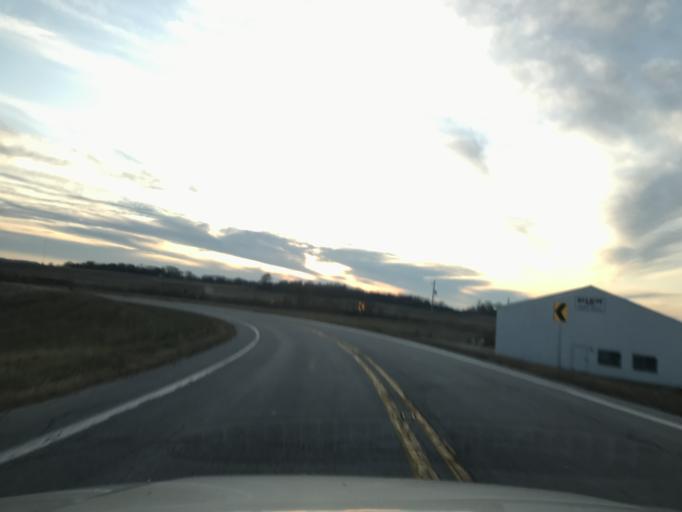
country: US
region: Illinois
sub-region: Henderson County
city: Oquawka
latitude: 41.0185
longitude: -90.8523
